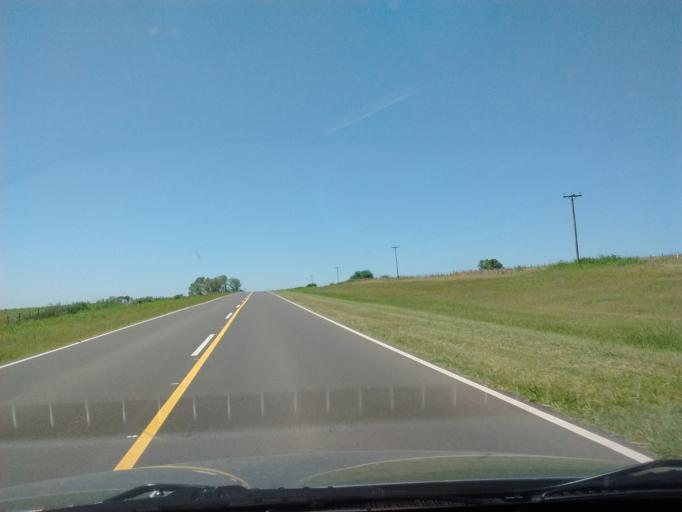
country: AR
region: Entre Rios
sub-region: Departamento de Victoria
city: Victoria
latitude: -32.8227
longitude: -59.8782
